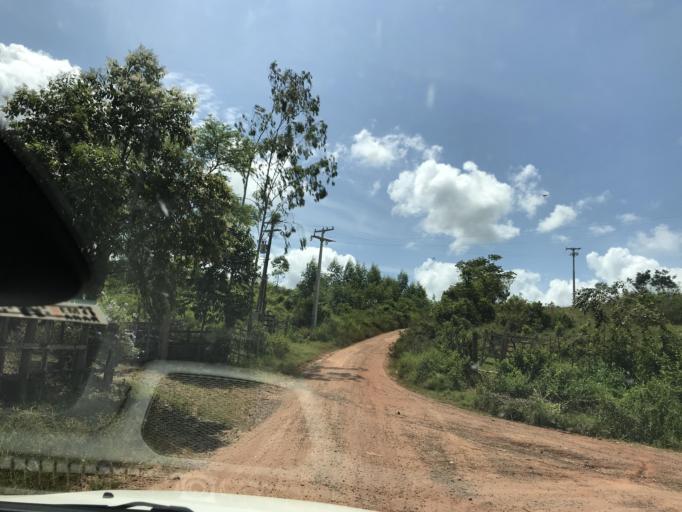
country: BR
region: Bahia
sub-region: Entre Rios
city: Entre Rios
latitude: -12.2182
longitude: -38.0763
